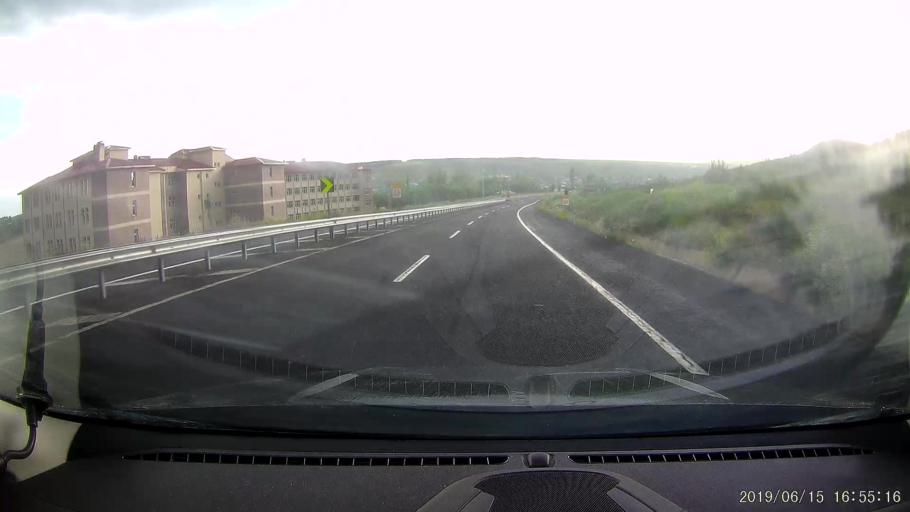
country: TR
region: Kars
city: Susuz
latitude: 40.7849
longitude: 43.1357
